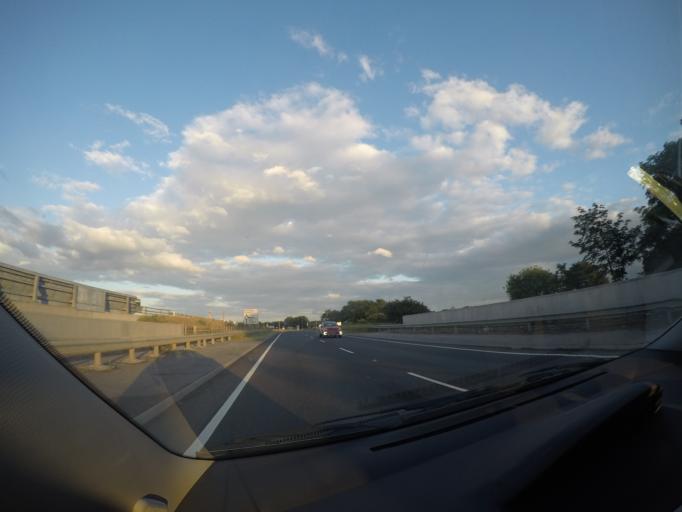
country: GB
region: England
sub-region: North Yorkshire
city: Bedale
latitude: 54.3014
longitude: -1.5680
